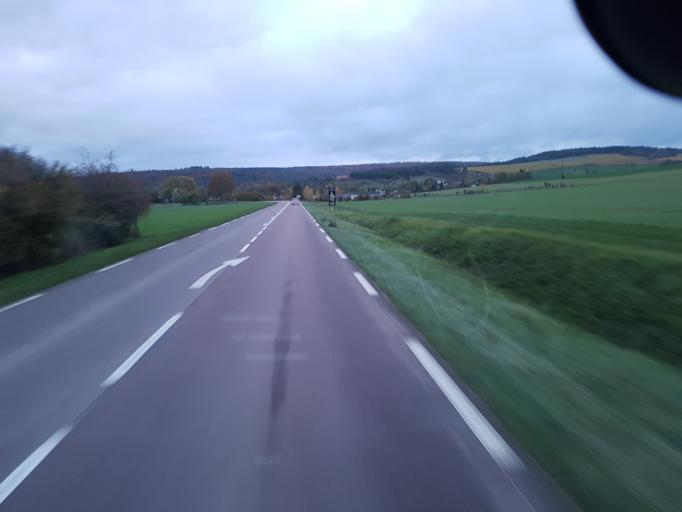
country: FR
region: Champagne-Ardenne
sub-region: Departement de l'Aube
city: Mussy-sur-Seine
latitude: 47.9681
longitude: 4.5003
